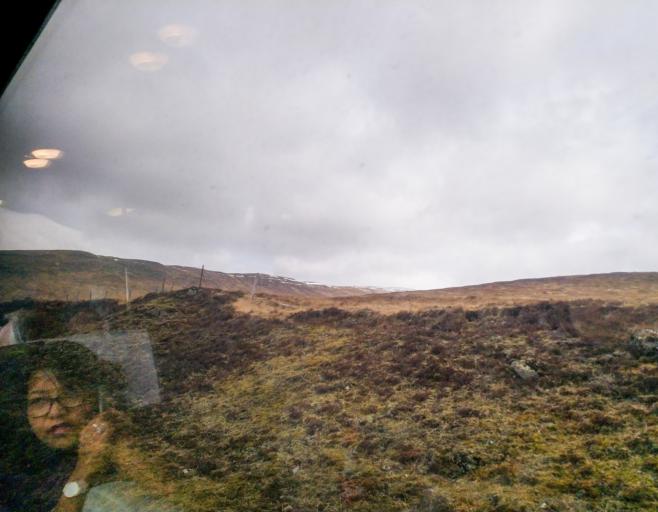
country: GB
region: Scotland
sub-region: Highland
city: Spean Bridge
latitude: 56.7678
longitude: -4.6999
